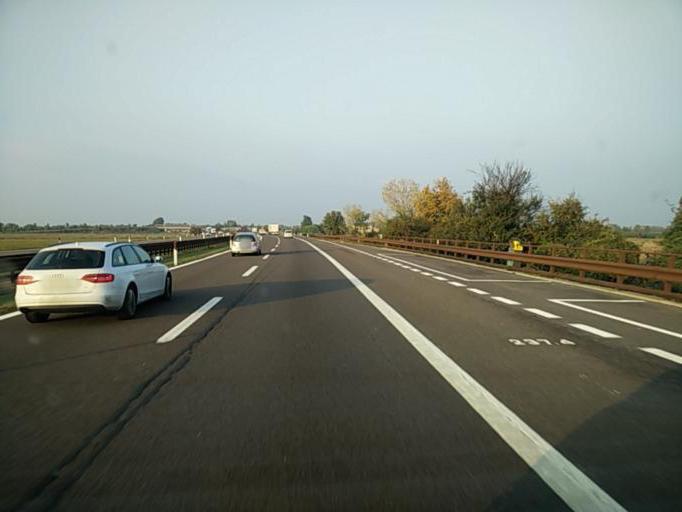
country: IT
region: Veneto
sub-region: Provincia di Verona
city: Vigasio
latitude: 45.3245
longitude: 10.9156
